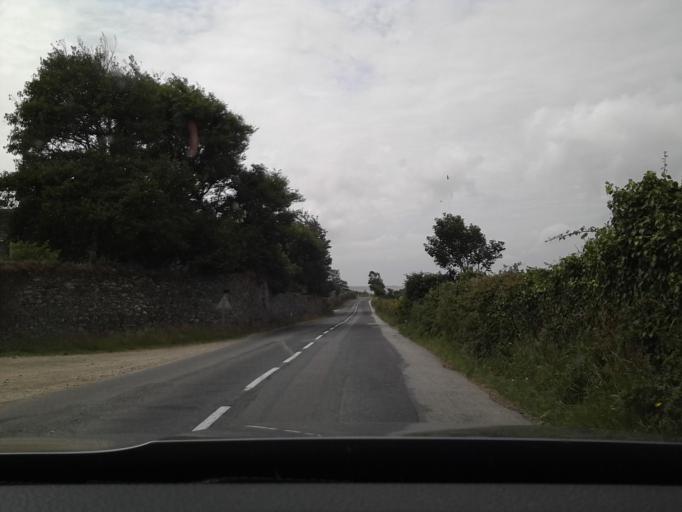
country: FR
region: Lower Normandy
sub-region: Departement de la Manche
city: Urville-Nacqueville
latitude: 49.6767
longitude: -1.7551
